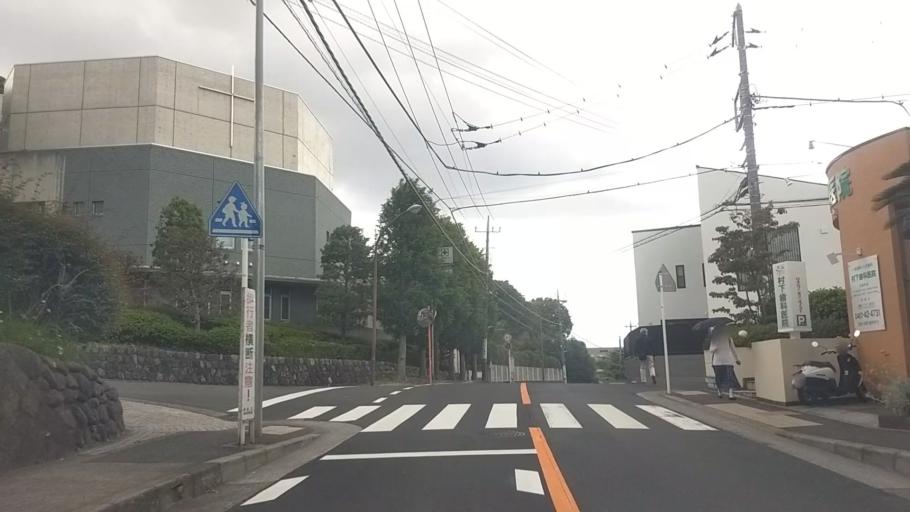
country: JP
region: Kanagawa
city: Fujisawa
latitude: 35.3565
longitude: 139.5208
